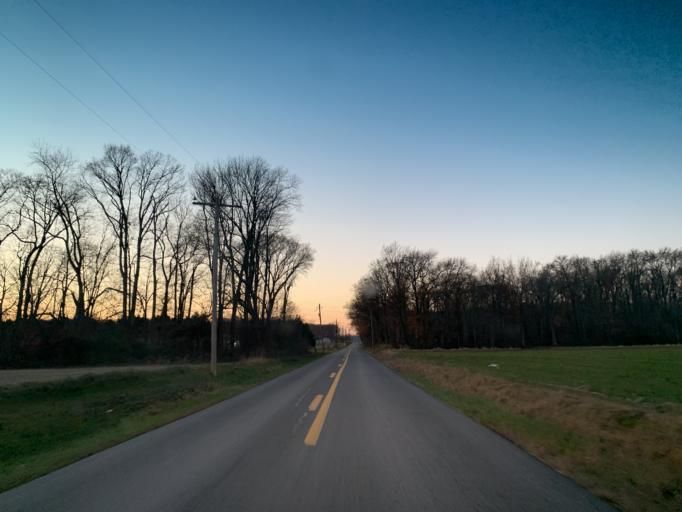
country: US
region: Delaware
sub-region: New Castle County
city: Middletown
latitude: 39.4130
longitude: -75.7590
